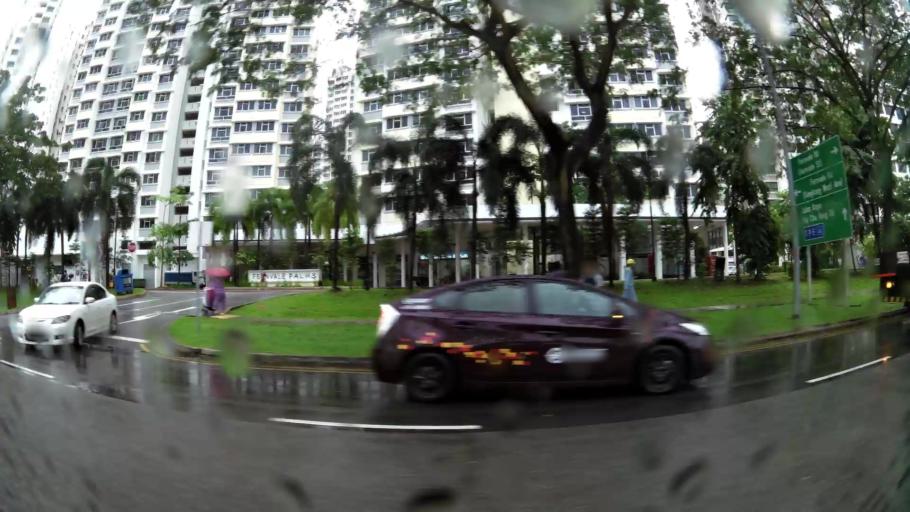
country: MY
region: Johor
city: Kampung Pasir Gudang Baru
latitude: 1.3952
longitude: 103.8770
